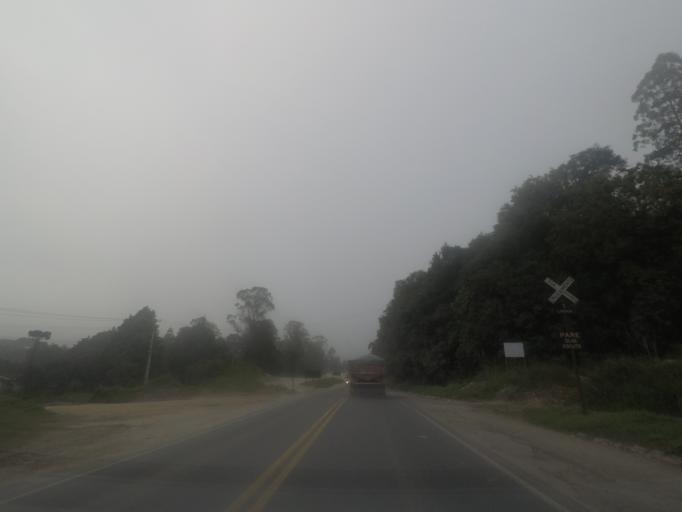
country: BR
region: Parana
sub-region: Almirante Tamandare
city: Almirante Tamandare
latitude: -25.2661
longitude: -49.3031
